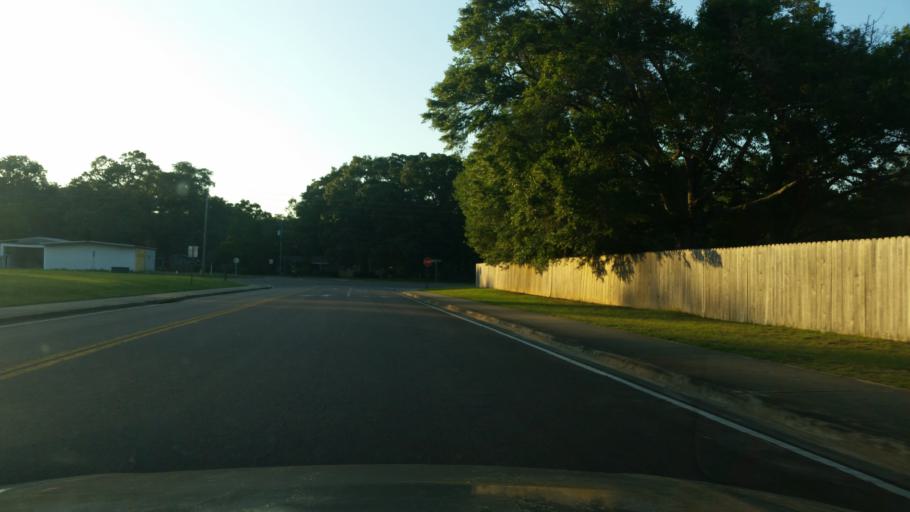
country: US
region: Florida
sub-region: Escambia County
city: Brent
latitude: 30.4792
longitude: -87.2344
